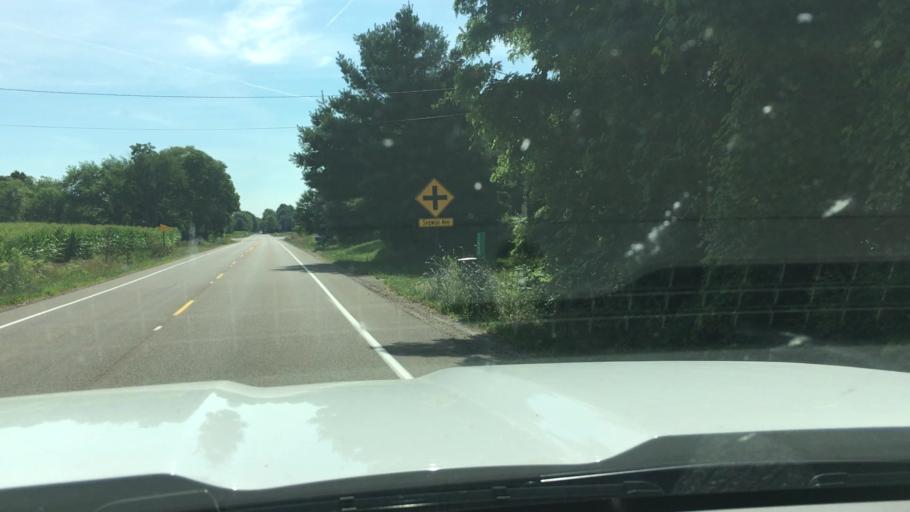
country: US
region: Michigan
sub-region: Kent County
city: Lowell
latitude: 42.8857
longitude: -85.3493
